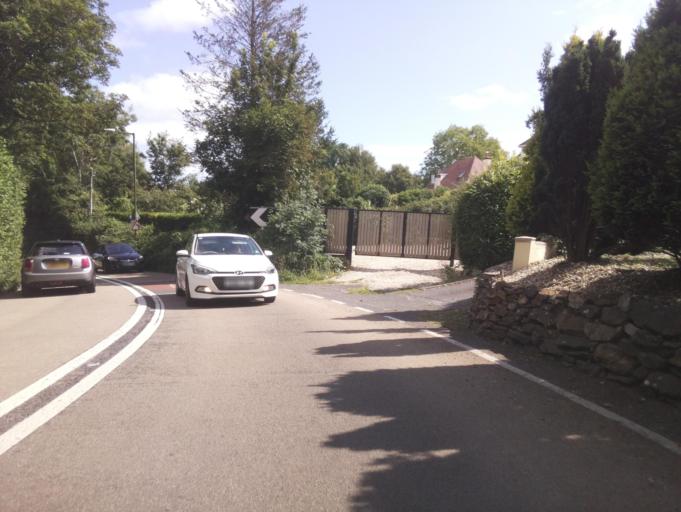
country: GB
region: England
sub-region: Borough of Torbay
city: Torquay
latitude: 50.5065
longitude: -3.5228
